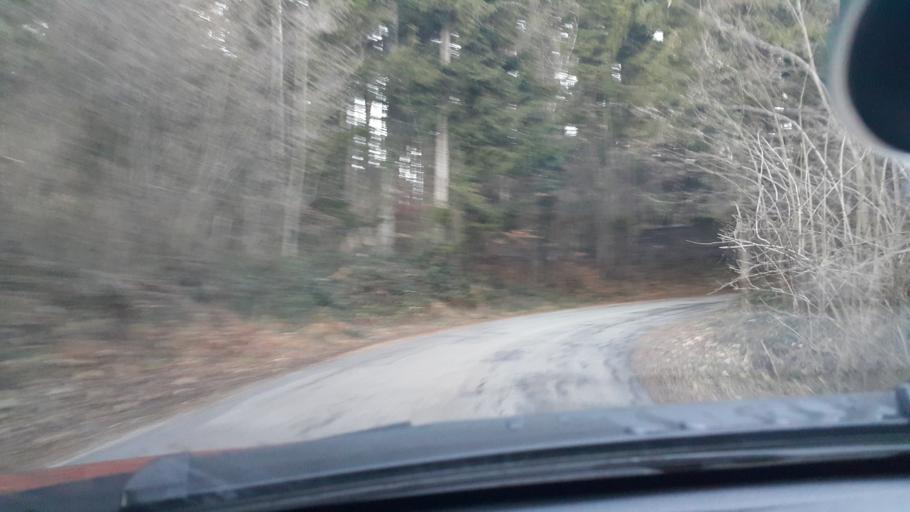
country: AT
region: Styria
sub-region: Politischer Bezirk Graz-Umgebung
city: Stiwoll
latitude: 47.1176
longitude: 15.2179
